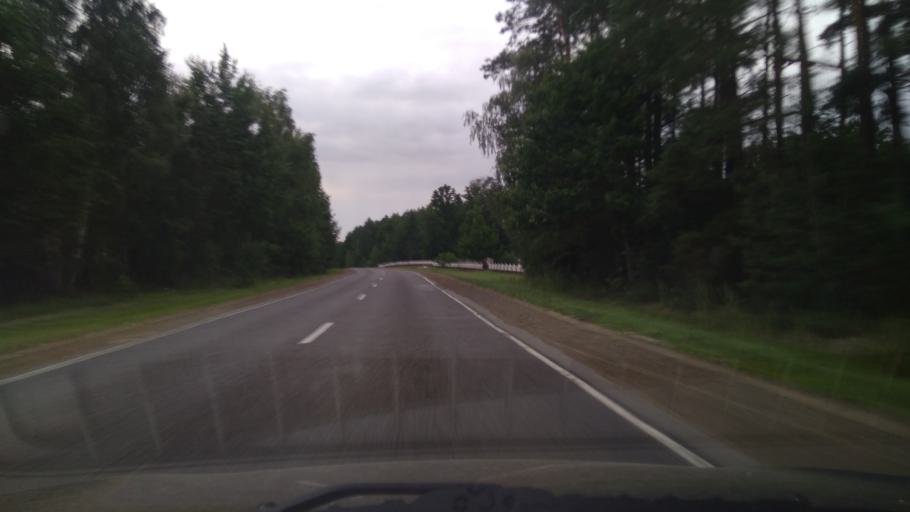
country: BY
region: Brest
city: Byaroza
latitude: 52.4042
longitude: 25.0008
